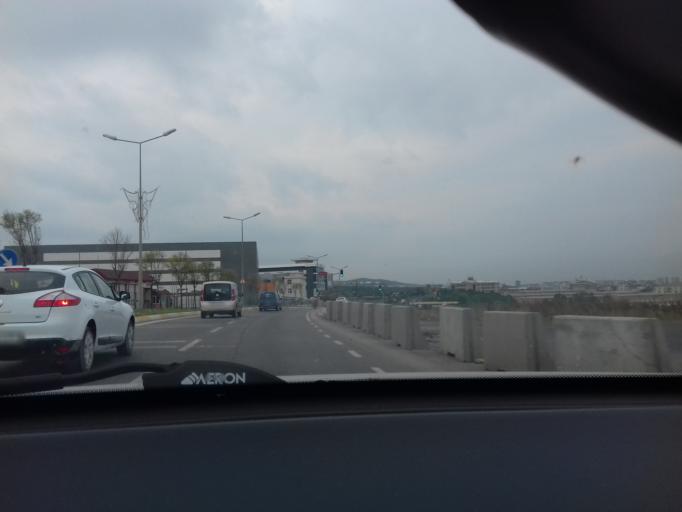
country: TR
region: Istanbul
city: Icmeler
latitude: 40.8870
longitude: 29.3523
